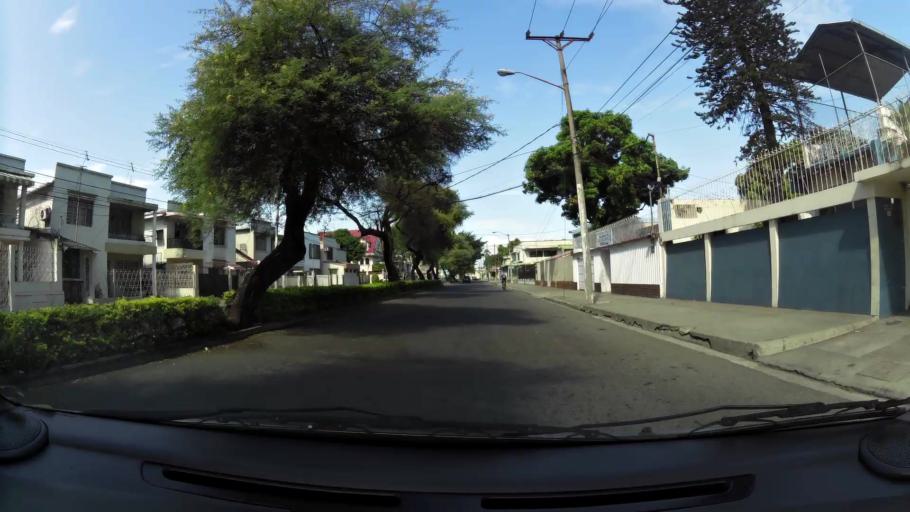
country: EC
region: Guayas
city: Guayaquil
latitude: -2.2199
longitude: -79.8958
